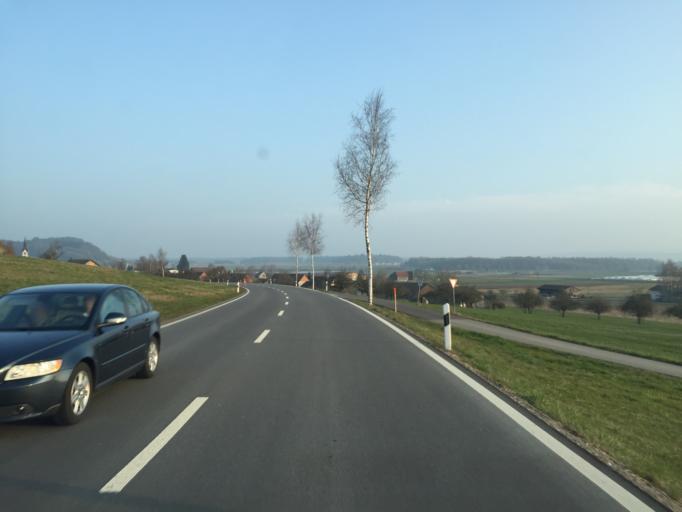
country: CH
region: Zurich
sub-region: Bezirk Andelfingen
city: Uhwiesen
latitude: 47.6563
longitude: 8.6455
